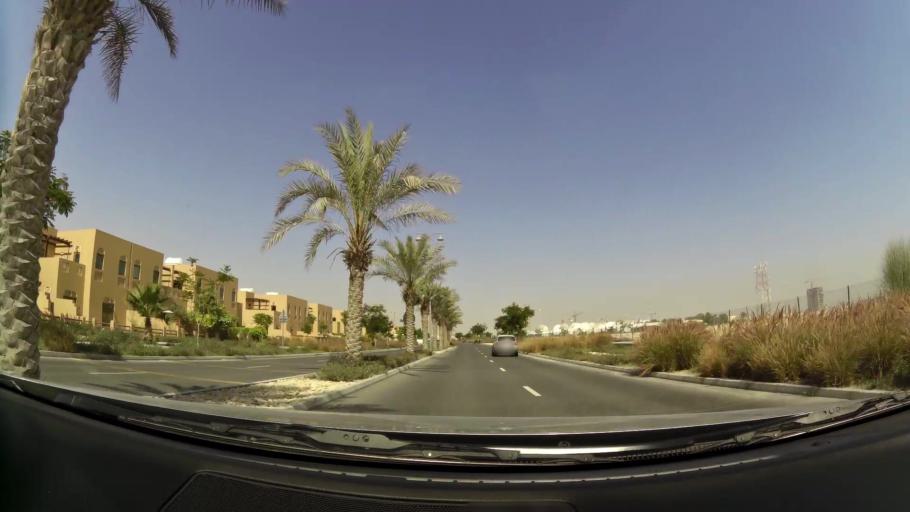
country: AE
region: Dubai
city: Dubai
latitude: 25.0229
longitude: 55.1458
